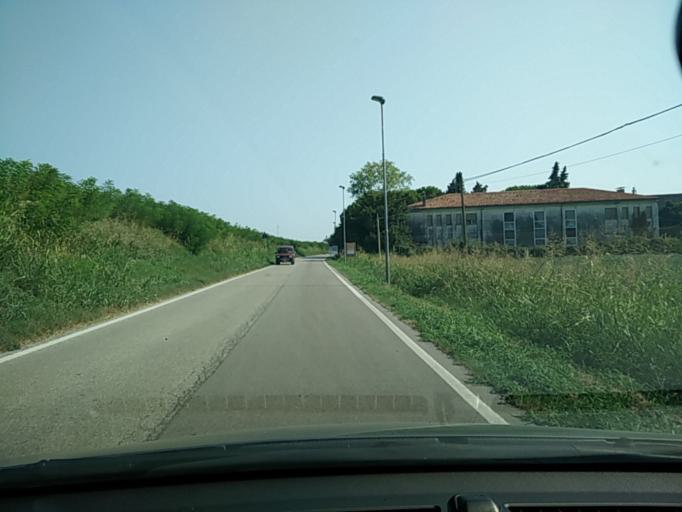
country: IT
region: Veneto
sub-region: Provincia di Venezia
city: Caorle
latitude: 45.6158
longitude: 12.8602
